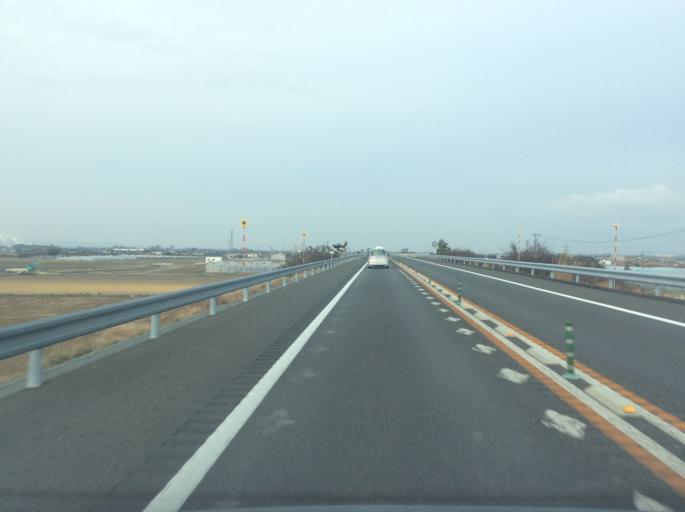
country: JP
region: Miyagi
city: Watari
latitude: 38.0254
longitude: 140.8897
